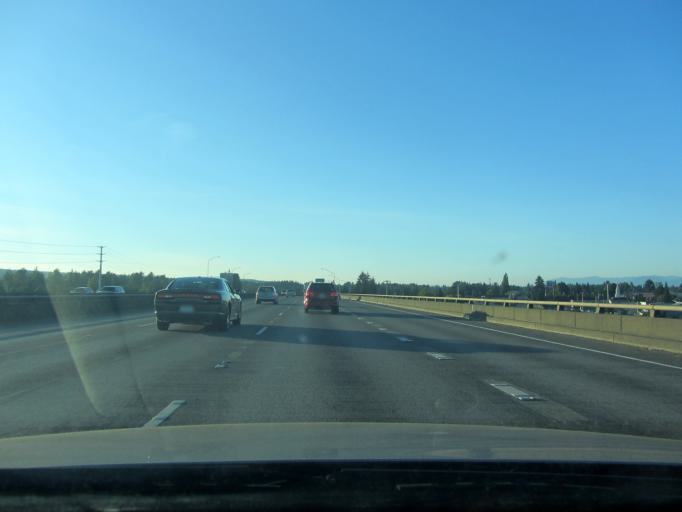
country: US
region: Washington
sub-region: Snohomish County
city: Marysville
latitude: 48.0465
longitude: -122.1824
